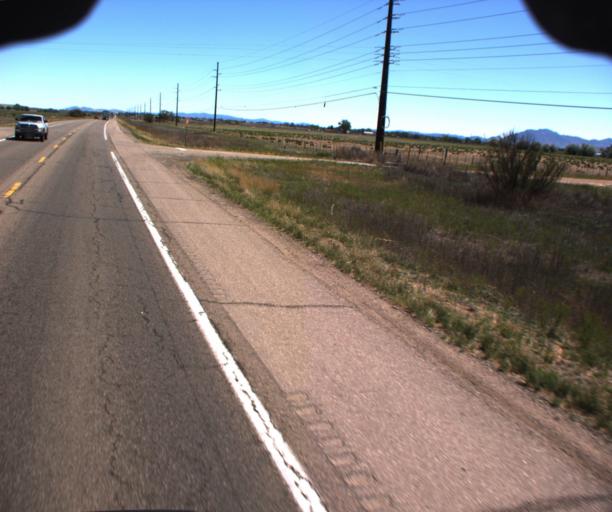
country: US
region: Arizona
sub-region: Yavapai County
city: Chino Valley
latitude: 34.8202
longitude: -112.4551
